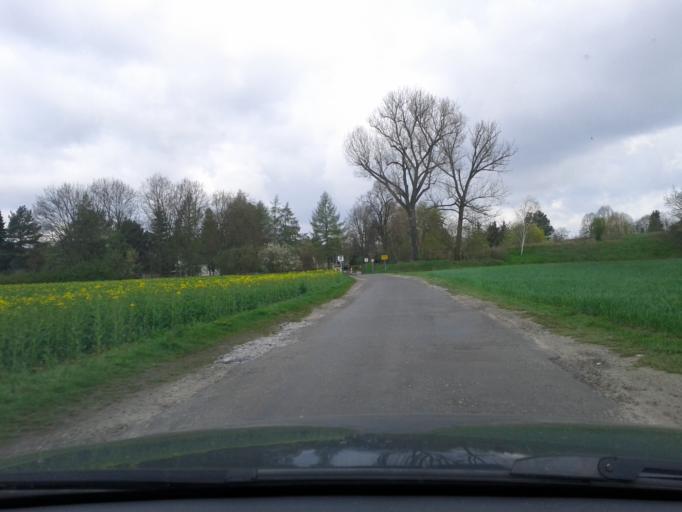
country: DE
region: Brandenburg
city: Schoneiche
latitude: 52.4861
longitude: 13.6739
